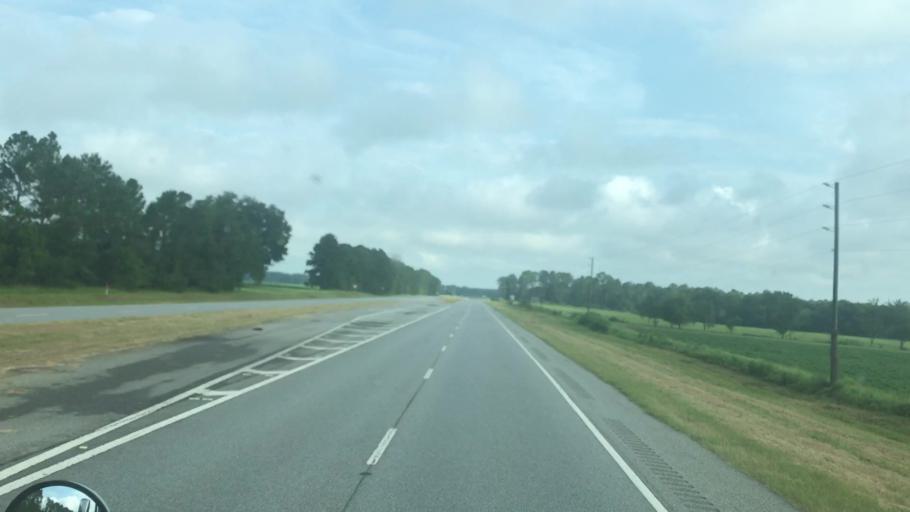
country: US
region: Georgia
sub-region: Miller County
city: Colquitt
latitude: 31.2074
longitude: -84.7726
